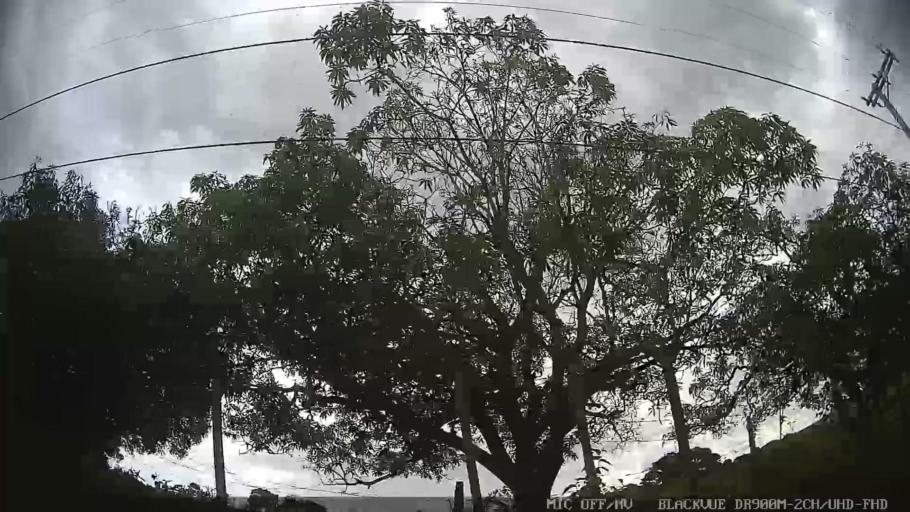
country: BR
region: Sao Paulo
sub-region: Jaguariuna
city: Jaguariuna
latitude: -22.6609
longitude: -46.9806
